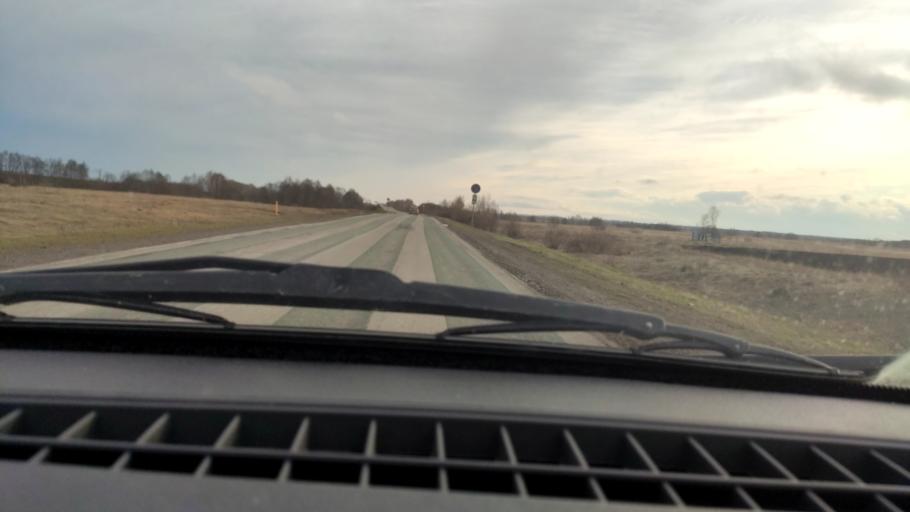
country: RU
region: Bashkortostan
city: Chishmy
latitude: 54.4454
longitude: 55.2432
